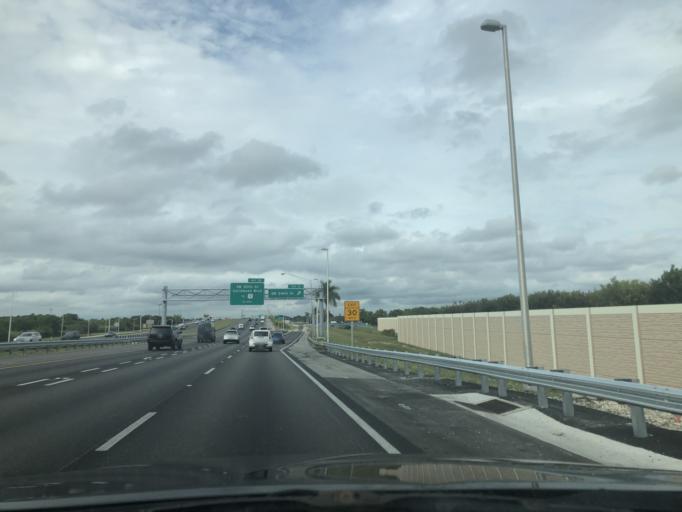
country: US
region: Florida
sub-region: Miami-Dade County
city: Goulds
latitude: 25.5610
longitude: -80.3622
